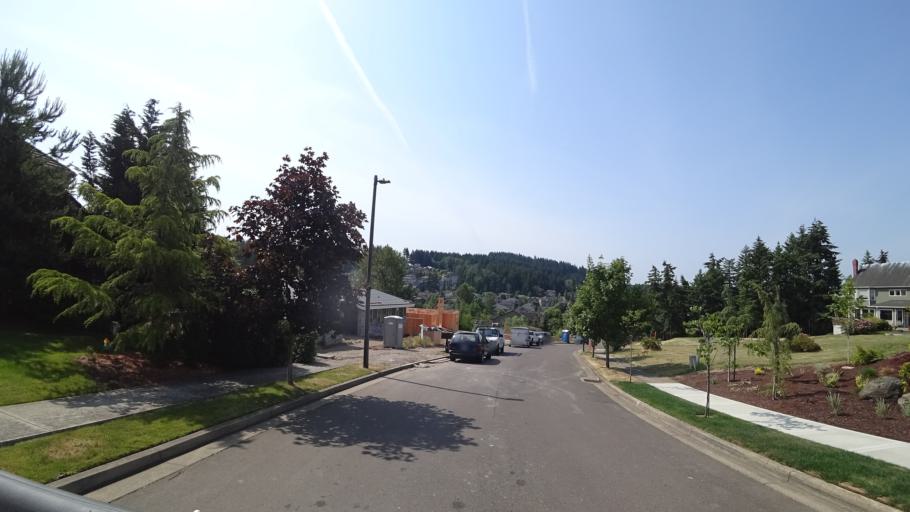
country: US
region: Oregon
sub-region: Clackamas County
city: Happy Valley
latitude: 45.4579
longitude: -122.5112
